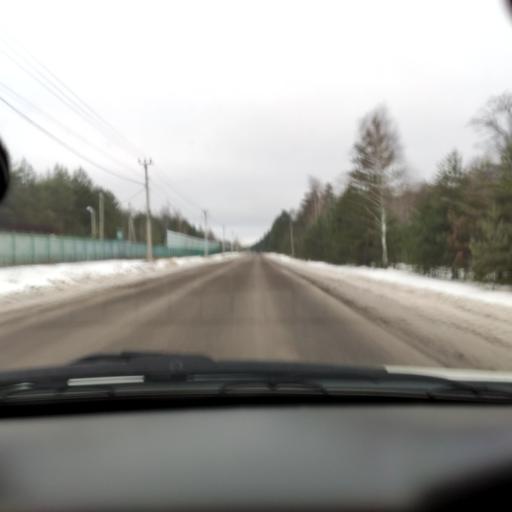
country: RU
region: Voronezj
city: Ramon'
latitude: 51.8913
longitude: 39.2445
